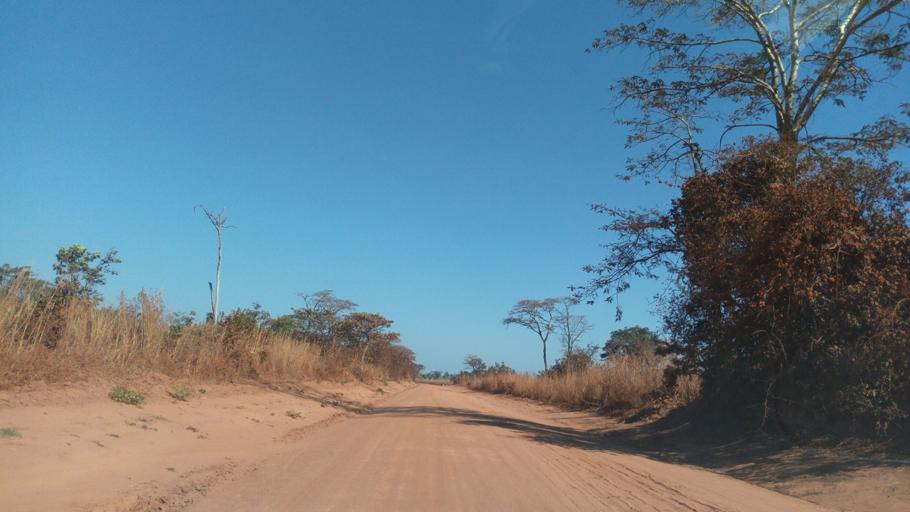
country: ZM
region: Luapula
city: Mwense
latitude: -10.7541
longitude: 28.3084
